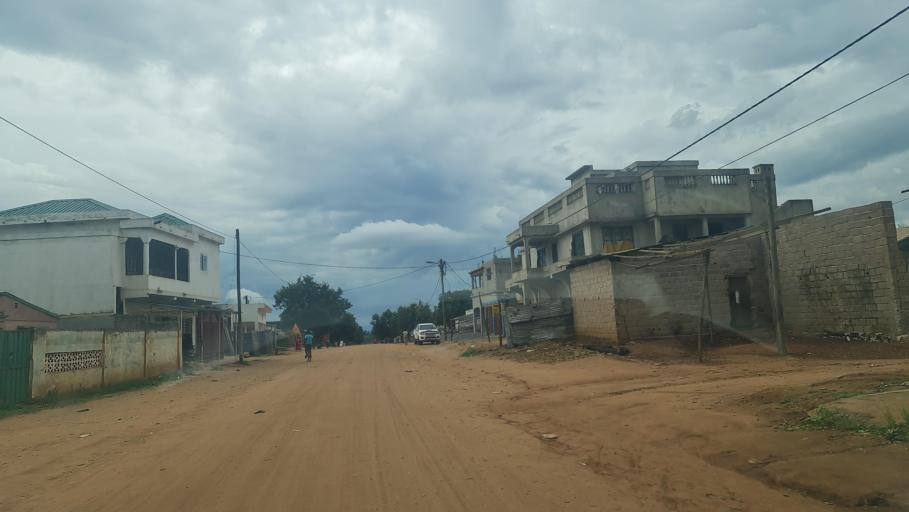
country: MW
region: Southern Region
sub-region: Nsanje District
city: Nsanje
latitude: -17.3308
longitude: 35.5934
